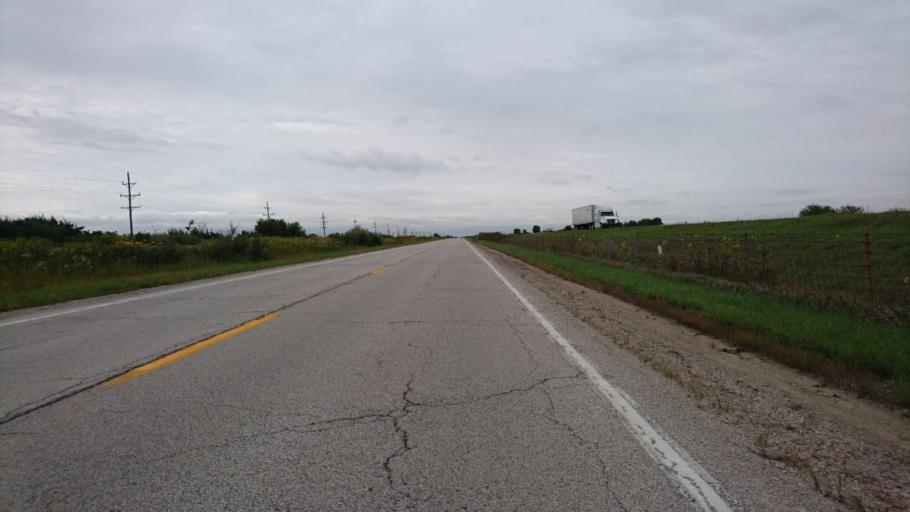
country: US
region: Illinois
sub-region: Livingston County
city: Odell
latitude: 41.0486
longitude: -88.4830
